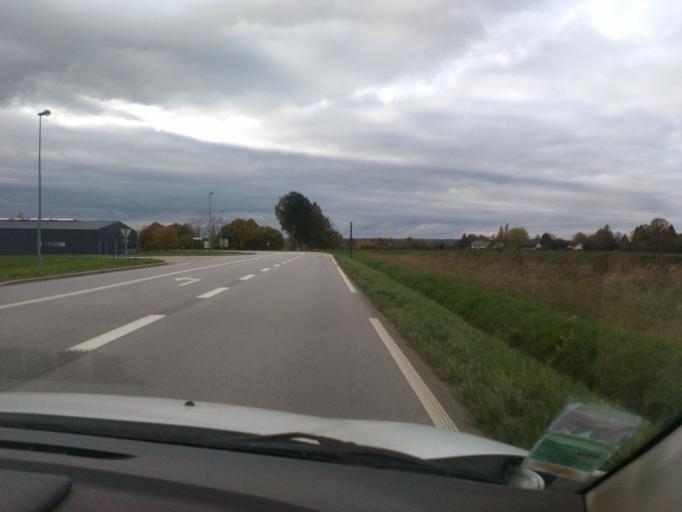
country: FR
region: Lorraine
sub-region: Departement des Vosges
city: Rambervillers
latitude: 48.3439
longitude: 6.6574
